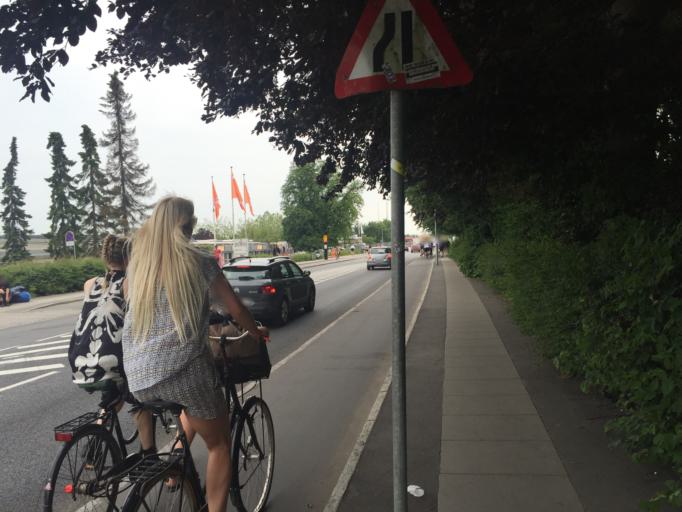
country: DK
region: Zealand
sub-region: Roskilde Kommune
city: Roskilde
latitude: 55.6272
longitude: 12.0786
